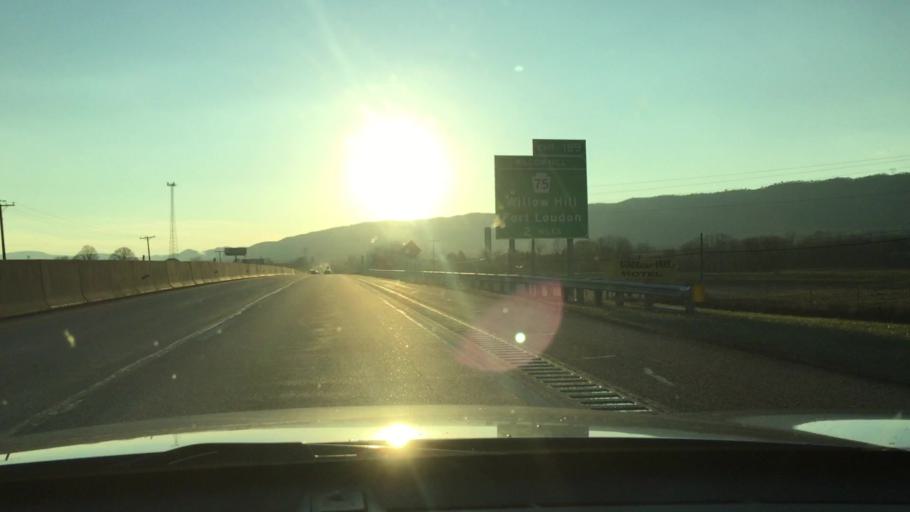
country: US
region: Pennsylvania
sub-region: Franklin County
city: Doylestown
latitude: 40.1170
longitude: -77.7833
